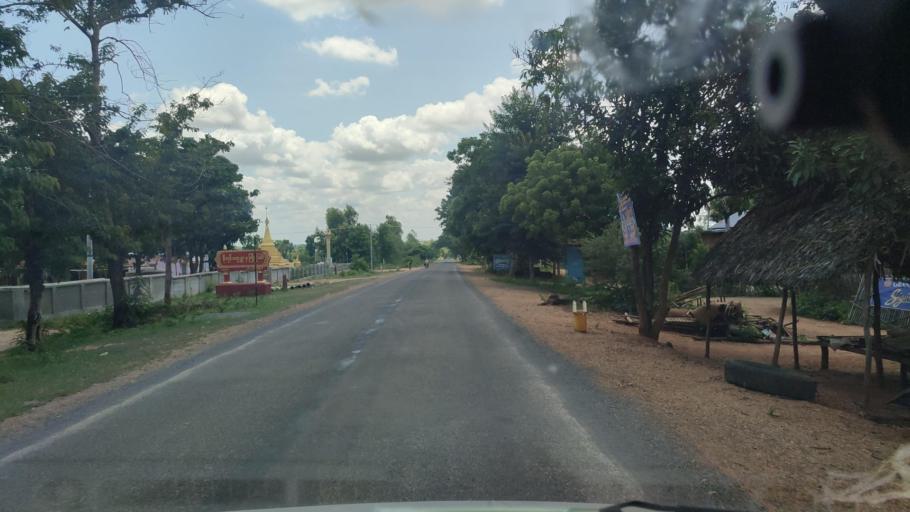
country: MM
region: Magway
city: Magway
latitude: 20.1885
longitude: 95.1266
